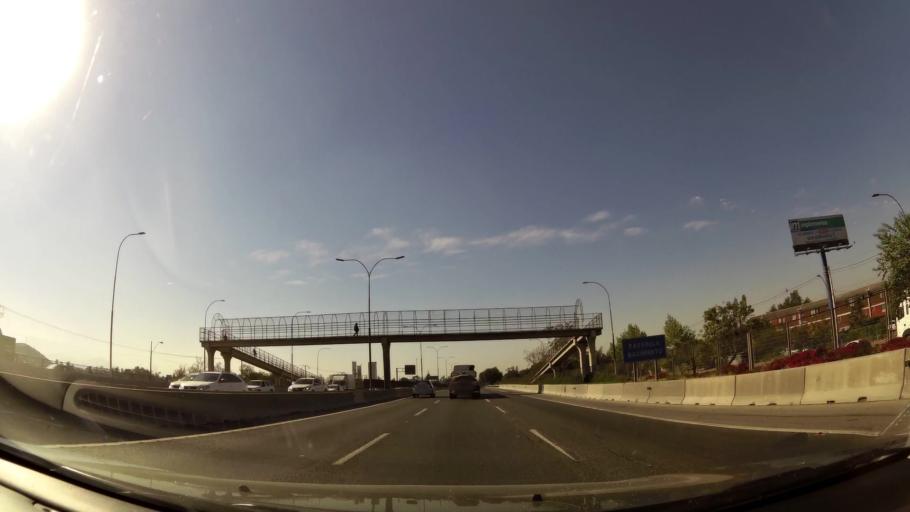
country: CL
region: Santiago Metropolitan
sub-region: Provincia de Maipo
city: San Bernardo
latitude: -33.5781
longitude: -70.7133
